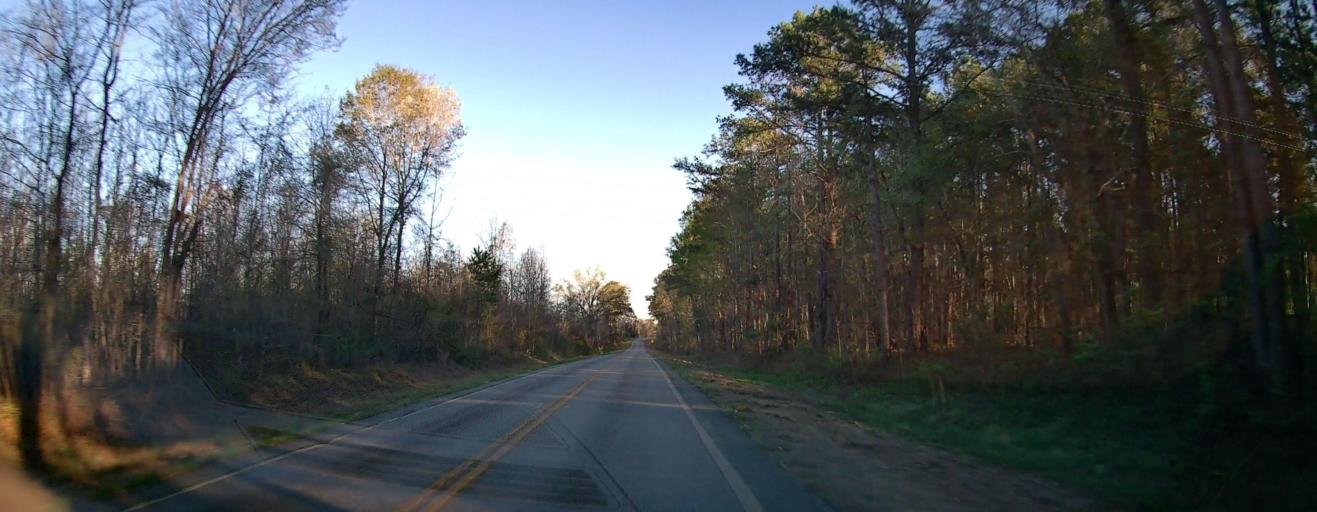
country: US
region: Georgia
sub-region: Wilcox County
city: Abbeville
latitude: 32.1060
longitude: -83.3106
